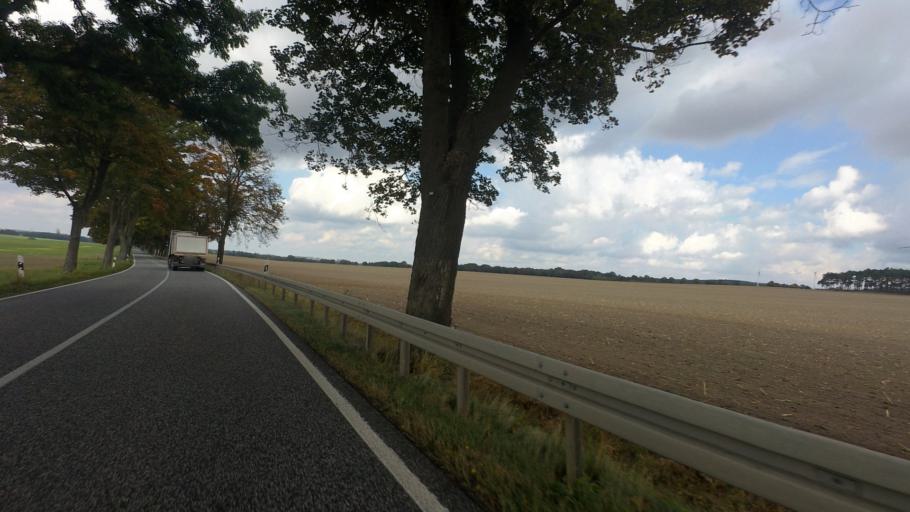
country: DE
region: Brandenburg
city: Juterbog
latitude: 51.9643
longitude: 13.1099
